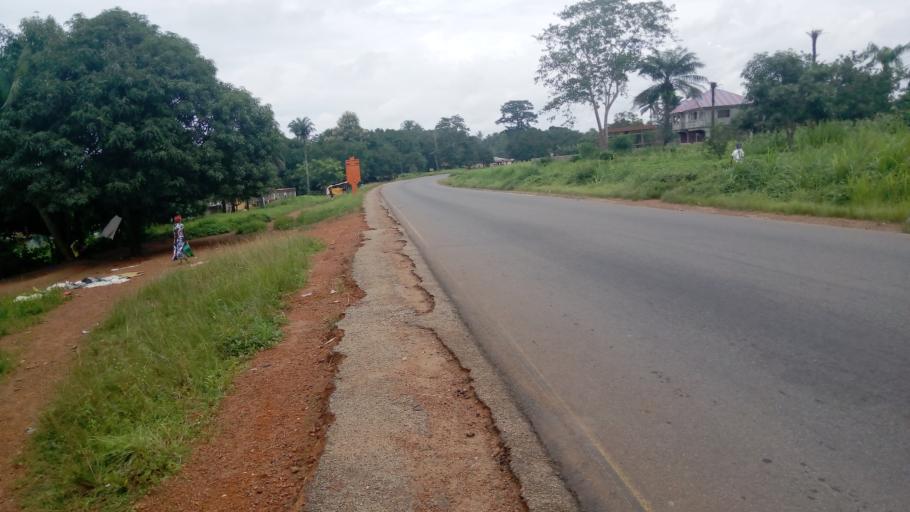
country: SL
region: Northern Province
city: Port Loko
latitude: 8.5043
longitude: -12.7597
